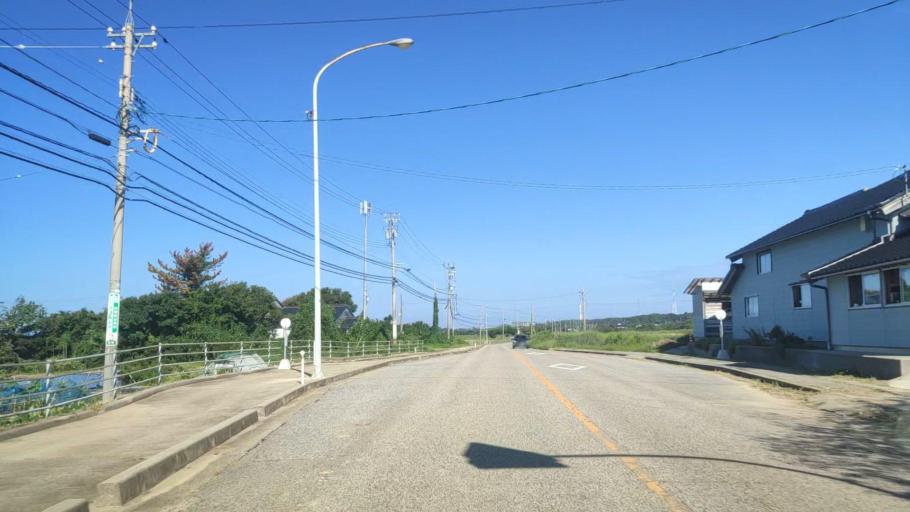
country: JP
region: Ishikawa
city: Hakui
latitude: 37.0386
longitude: 136.7431
